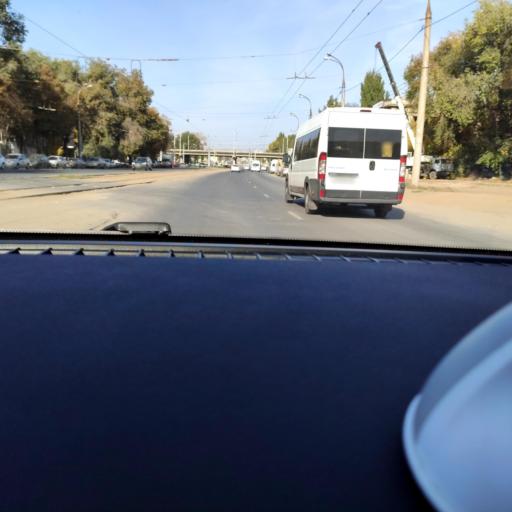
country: RU
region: Samara
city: Smyshlyayevka
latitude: 53.2057
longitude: 50.2794
